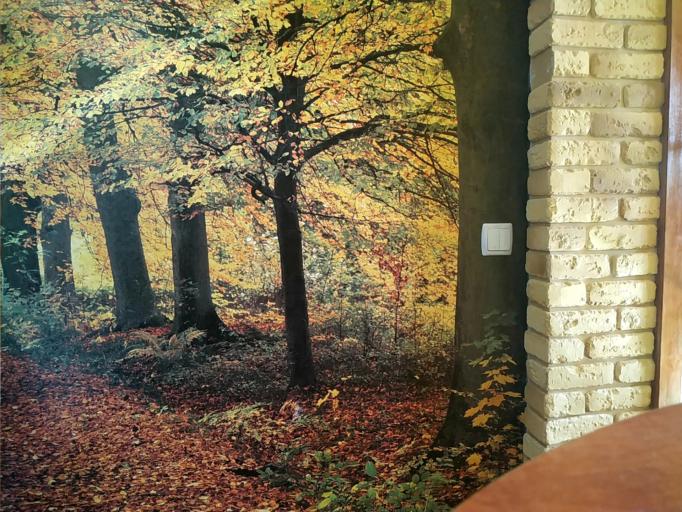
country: RU
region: Jaroslavl
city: Kukoboy
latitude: 58.8259
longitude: 39.7596
